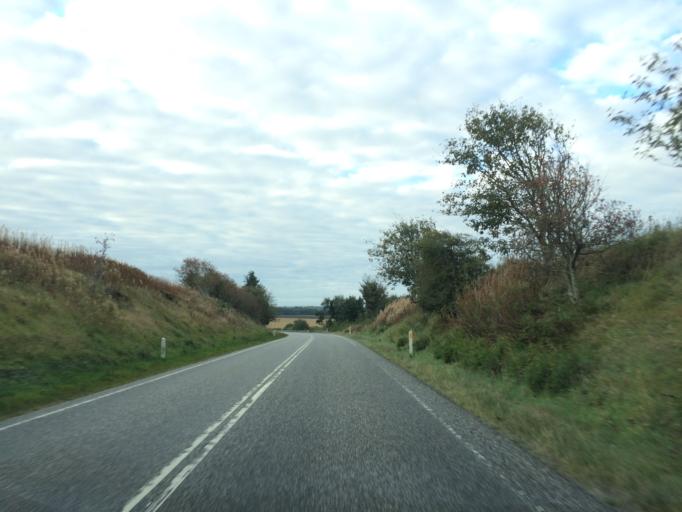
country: DK
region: Central Jutland
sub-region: Ringkobing-Skjern Kommune
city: Skjern
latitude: 56.0026
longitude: 8.5030
